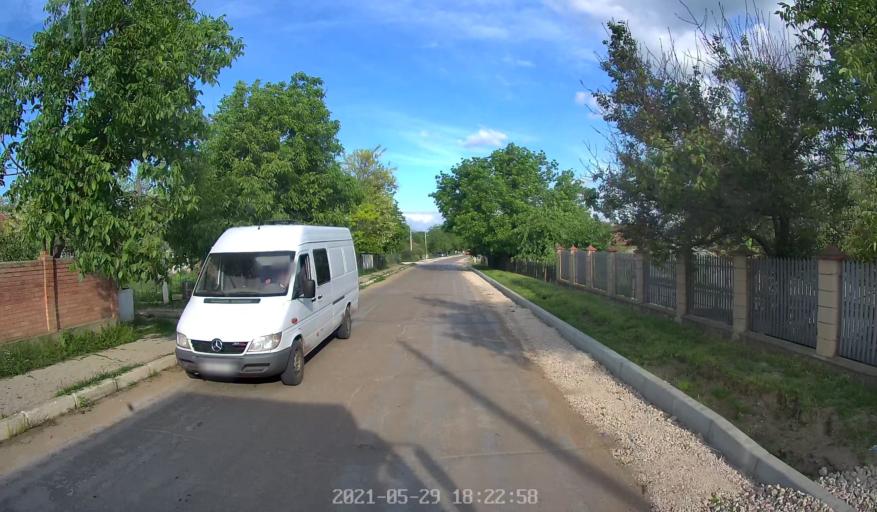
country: MD
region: Laloveni
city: Ialoveni
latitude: 46.8349
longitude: 28.8519
